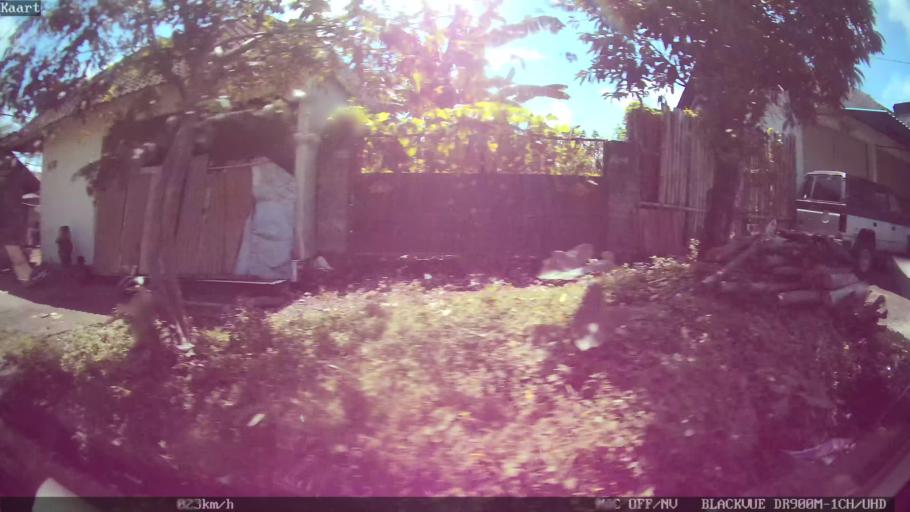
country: ID
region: Bali
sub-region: Kabupaten Gianyar
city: Ubud
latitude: -8.5608
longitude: 115.3173
